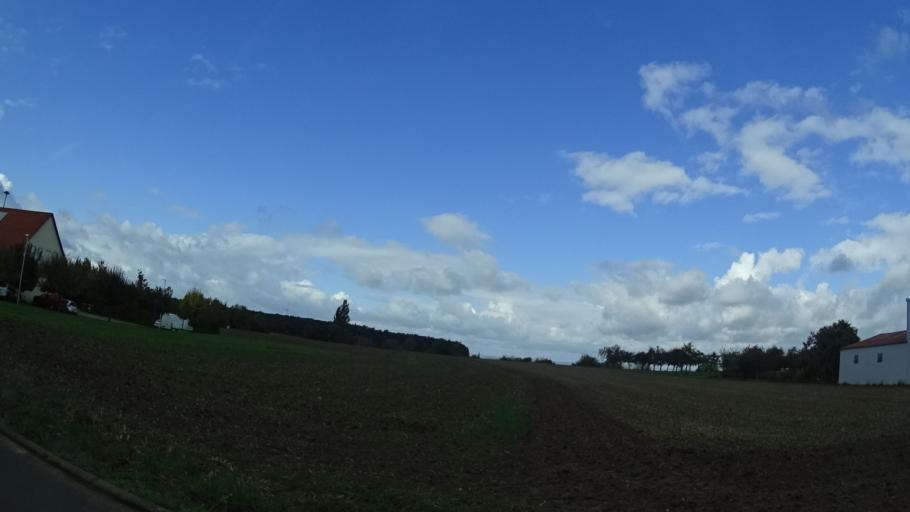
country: DE
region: Bavaria
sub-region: Regierungsbezirk Unterfranken
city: Lulsfeld
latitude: 49.8681
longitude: 10.3236
